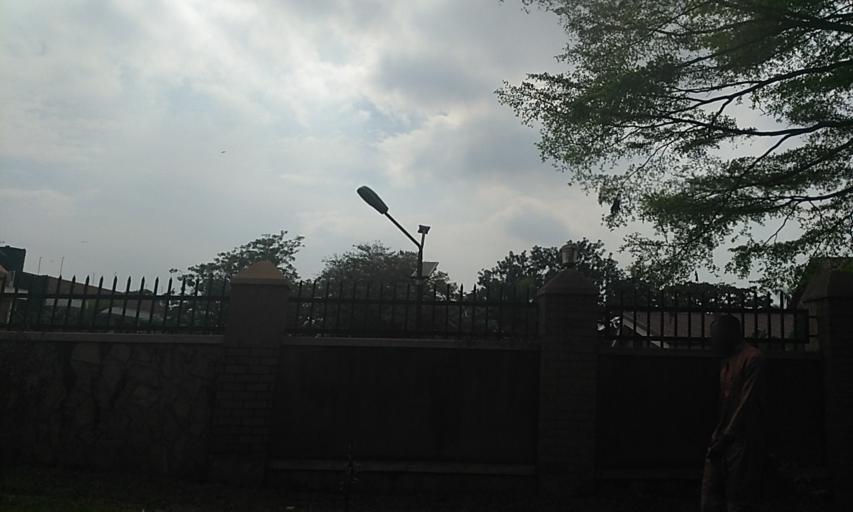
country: UG
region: Central Region
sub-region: Kampala District
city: Kampala
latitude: 0.2961
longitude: 32.5590
